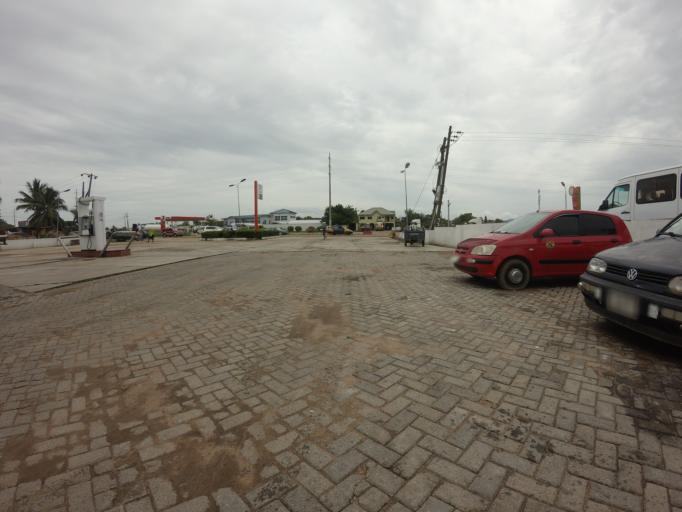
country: GH
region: Greater Accra
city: Achiaman
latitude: 5.7308
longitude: -0.3123
